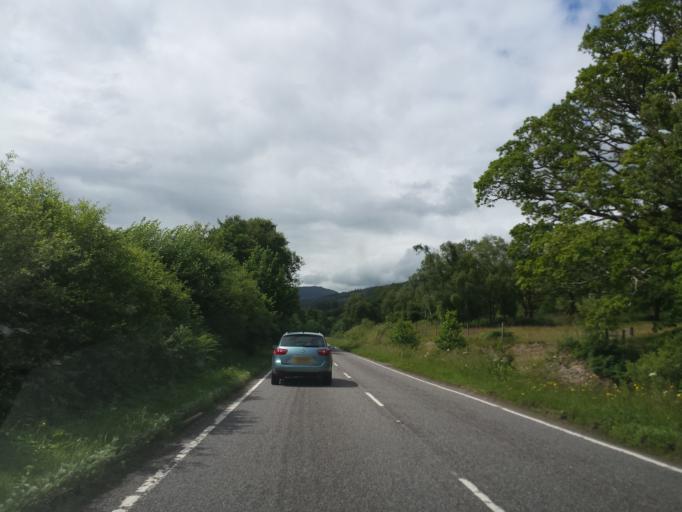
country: GB
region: Scotland
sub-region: Highland
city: Fort William
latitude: 56.8501
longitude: -5.1677
